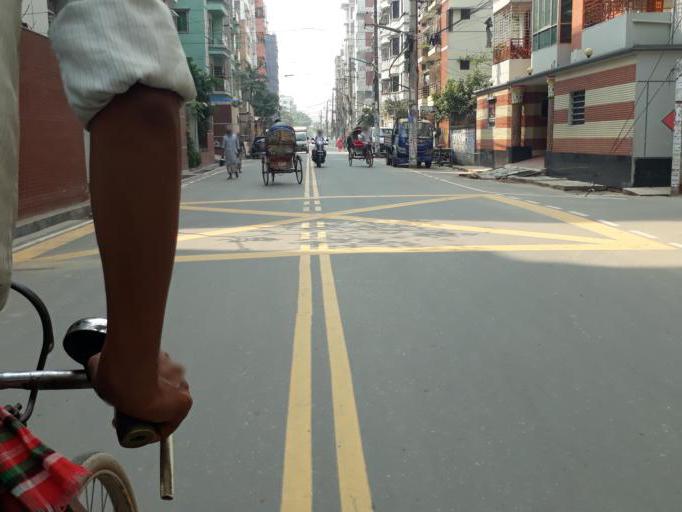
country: BD
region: Dhaka
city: Tungi
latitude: 23.8766
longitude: 90.3840
